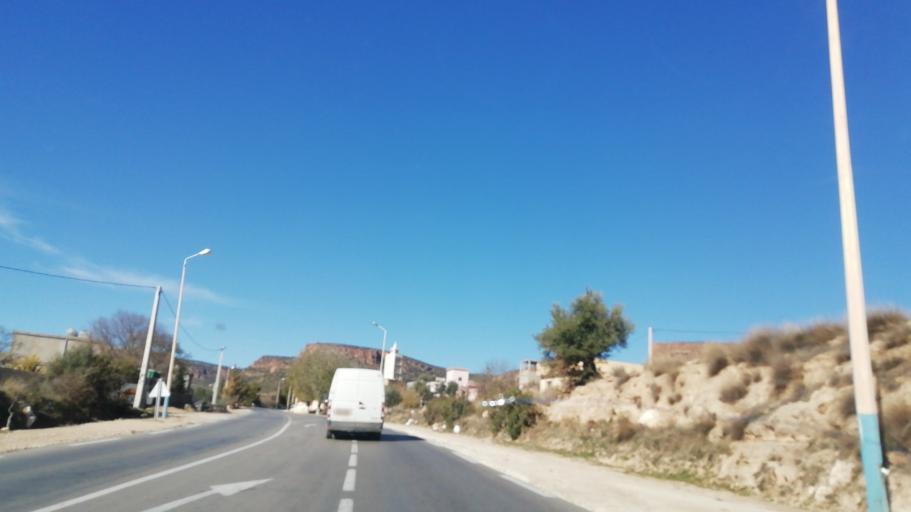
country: DZ
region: Tlemcen
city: Sebdou
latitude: 34.6793
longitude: -1.3143
